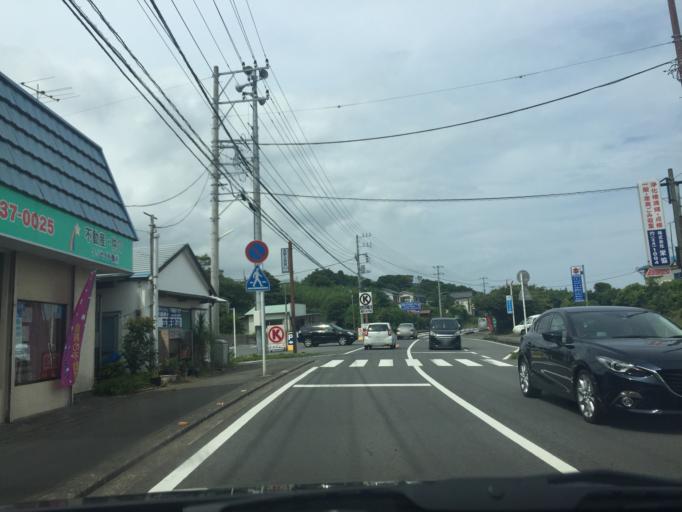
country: JP
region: Shizuoka
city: Shimoda
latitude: 34.7619
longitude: 139.0205
